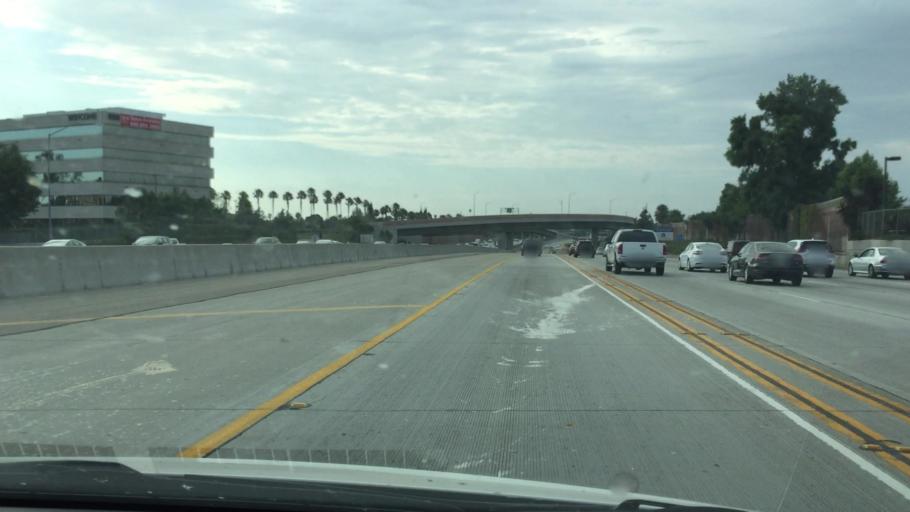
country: US
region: California
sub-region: Orange County
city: Anaheim
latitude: 33.8201
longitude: -117.9201
